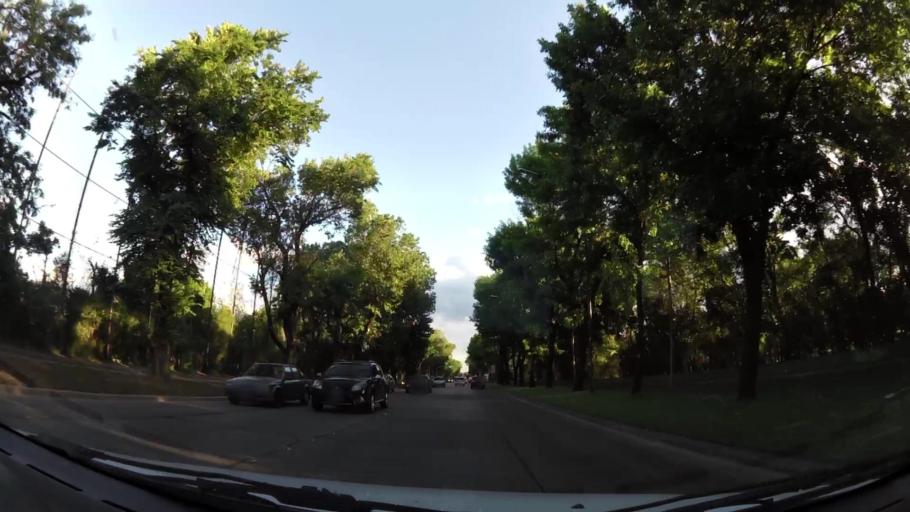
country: AR
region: Buenos Aires
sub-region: Partido de San Isidro
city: San Isidro
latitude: -34.4852
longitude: -58.5265
